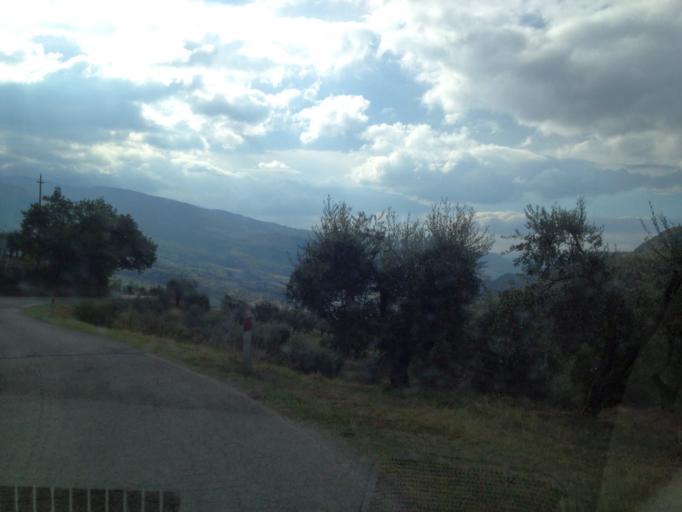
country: IT
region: Tuscany
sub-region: Province of Florence
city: Montebonello
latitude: 43.8592
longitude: 11.4979
